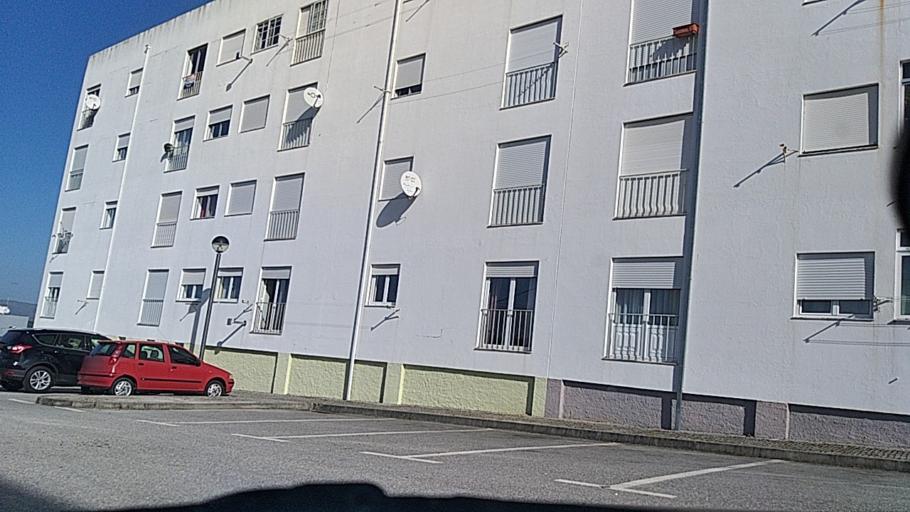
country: PT
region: Guarda
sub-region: Celorico da Beira
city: Celorico da Beira
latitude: 40.6410
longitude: -7.3919
